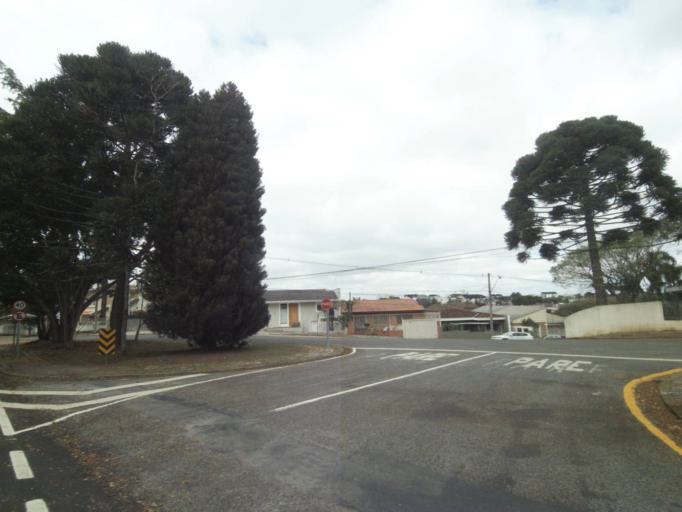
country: BR
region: Parana
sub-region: Curitiba
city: Curitiba
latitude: -25.4491
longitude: -49.3093
